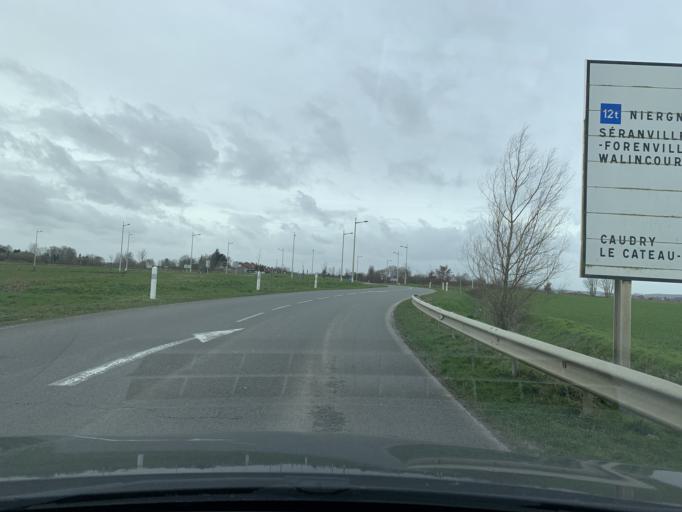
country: FR
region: Nord-Pas-de-Calais
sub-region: Departement du Nord
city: Cambrai
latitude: 50.1527
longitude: 3.2662
